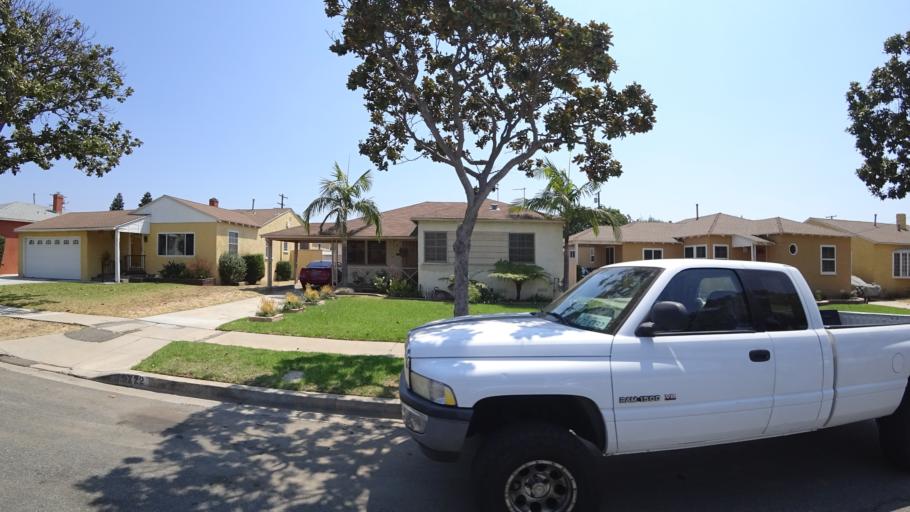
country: US
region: California
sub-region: Los Angeles County
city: Westmont
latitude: 33.9470
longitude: -118.3243
